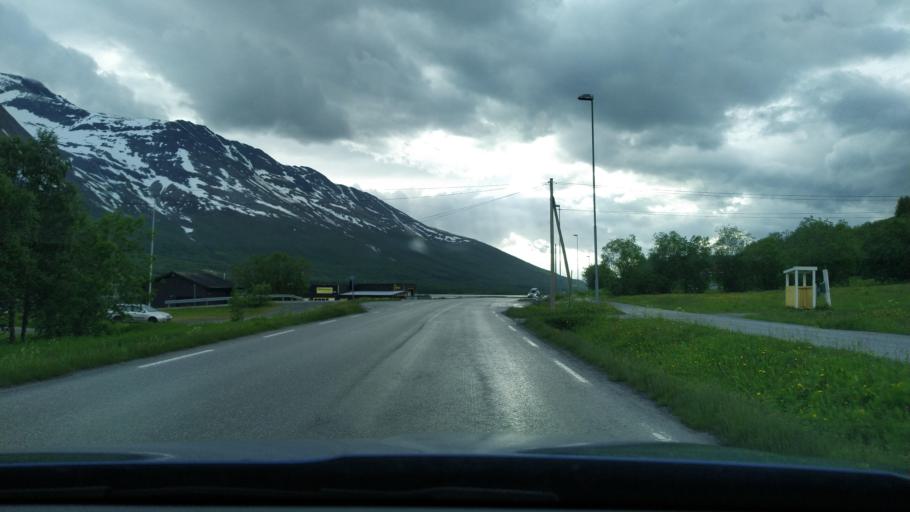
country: NO
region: Troms
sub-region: Balsfjord
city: Storsteinnes
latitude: 69.2201
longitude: 19.5399
